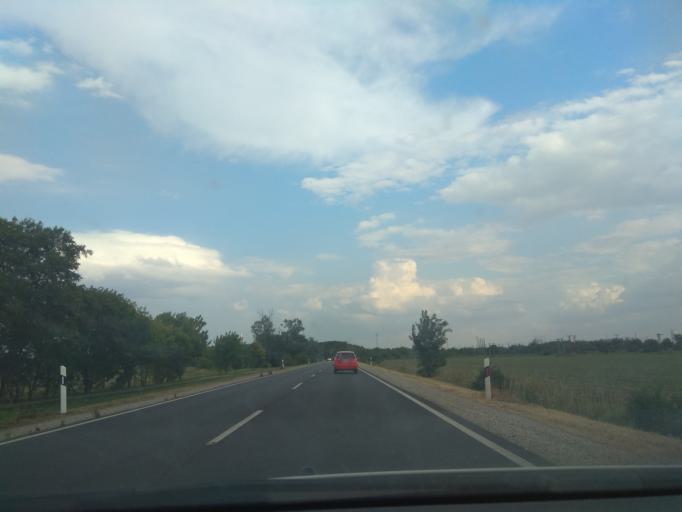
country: HU
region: Borsod-Abauj-Zemplen
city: Sajoszoged
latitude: 47.9334
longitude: 21.0166
